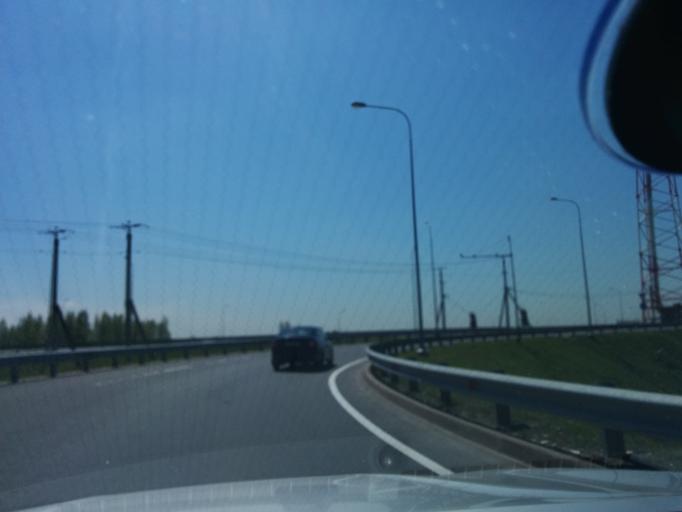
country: RU
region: Leningrad
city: Luppolovo
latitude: 60.1759
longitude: 30.3613
